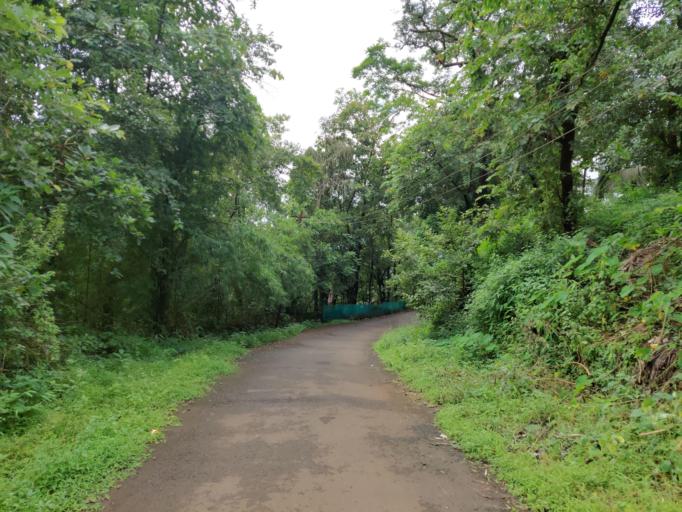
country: IN
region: Maharashtra
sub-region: Ratnagiri
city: Chiplun
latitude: 17.5571
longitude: 73.5073
